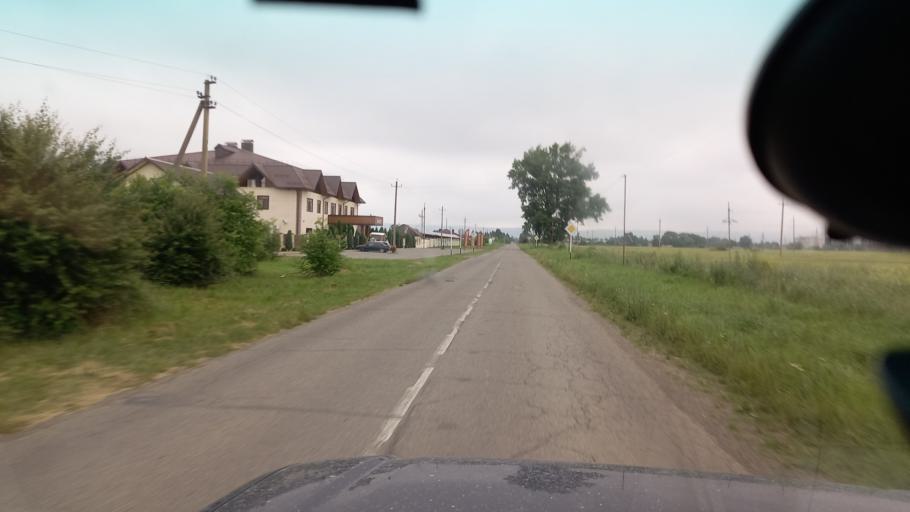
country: RU
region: Krasnodarskiy
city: Mostovskoy
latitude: 44.4231
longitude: 40.7594
